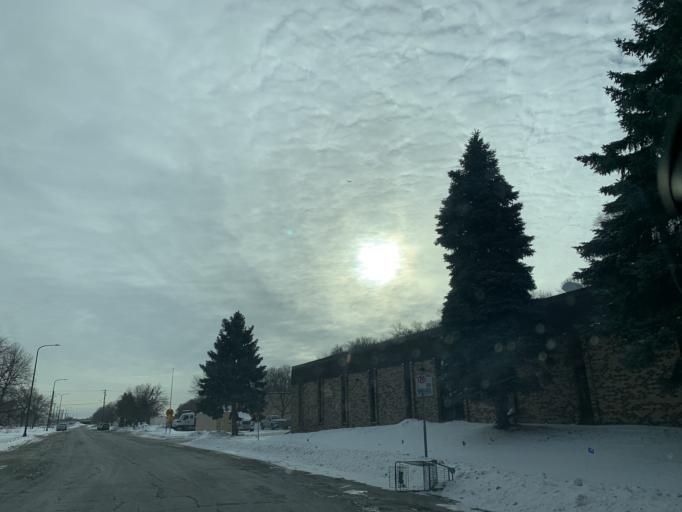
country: US
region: Minnesota
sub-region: Ramsey County
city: Saint Paul
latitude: 44.9357
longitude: -93.0786
